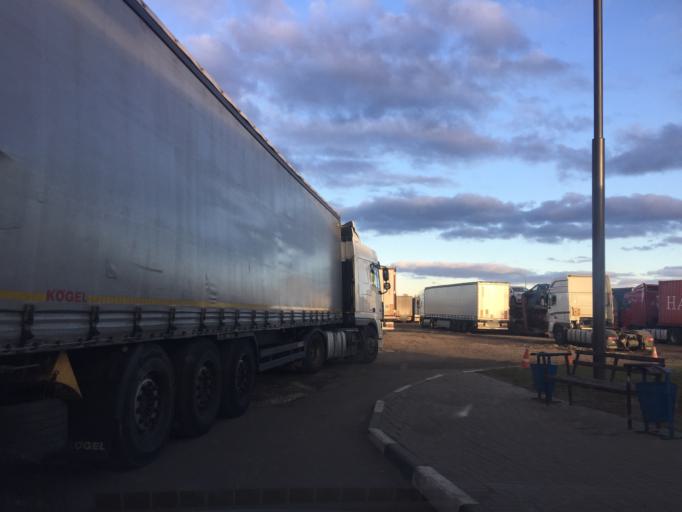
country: BY
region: Vitebsk
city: Myory
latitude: 55.8147
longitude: 27.6706
